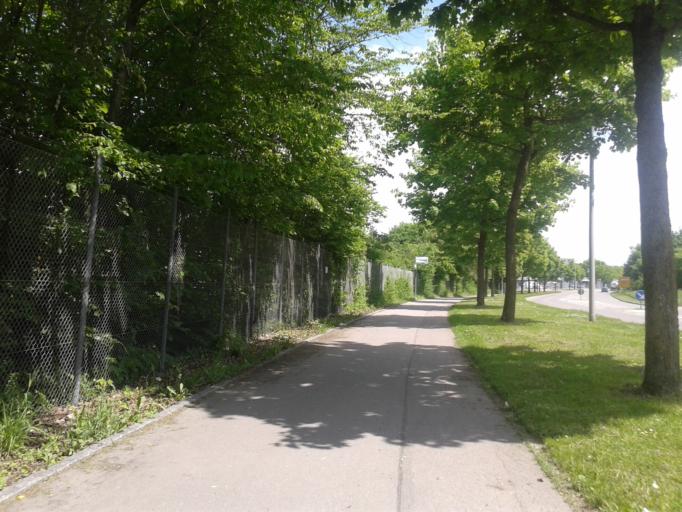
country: DE
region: Baden-Wuerttemberg
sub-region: Tuebingen Region
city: Ulm
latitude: 48.3607
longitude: 9.9535
